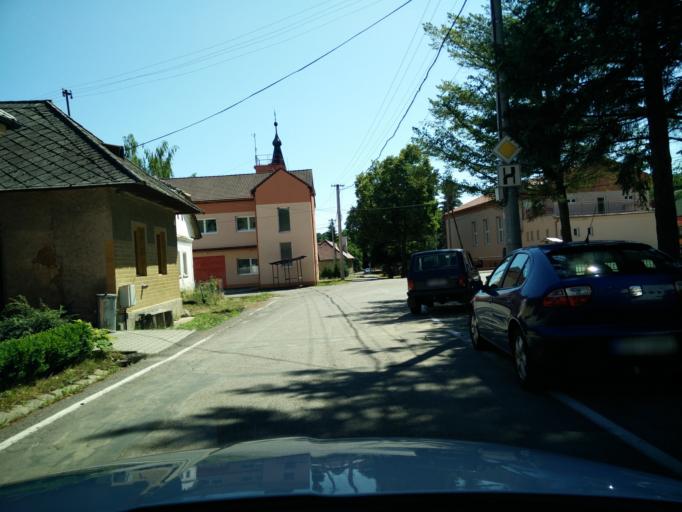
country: SK
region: Nitriansky
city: Prievidza
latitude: 48.7997
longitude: 18.7013
